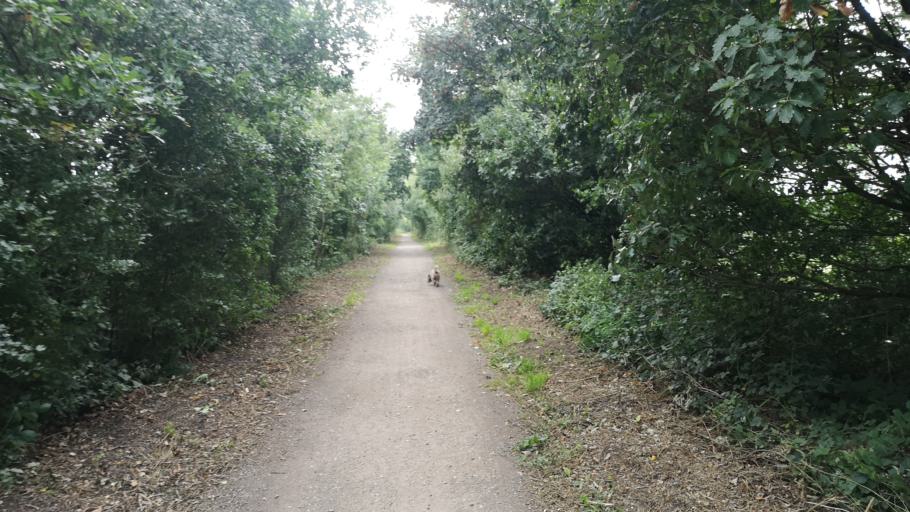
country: GB
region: England
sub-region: City and Borough of Wakefield
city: Notton
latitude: 53.6199
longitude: -1.4672
